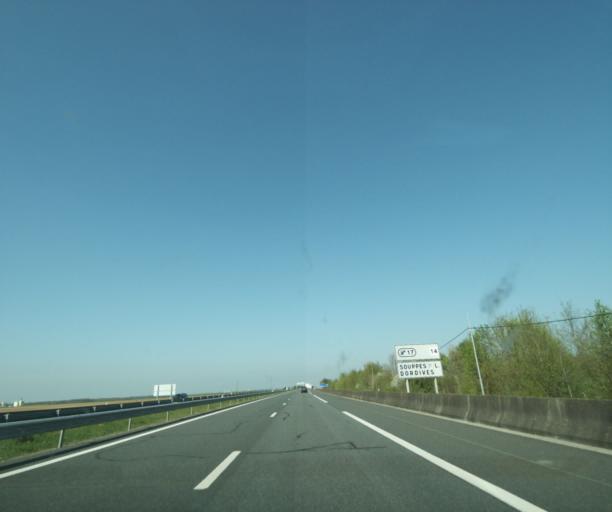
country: FR
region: Centre
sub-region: Departement du Loiret
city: Corquilleroy
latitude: 48.0663
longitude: 2.6739
